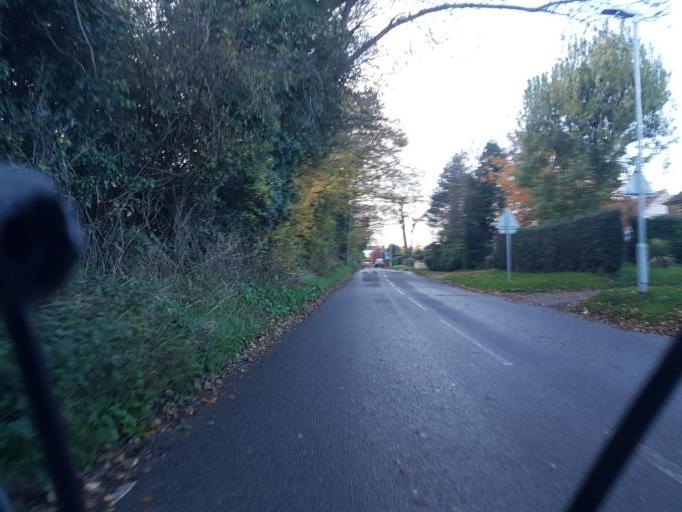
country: GB
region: England
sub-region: Kent
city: Sittingbourne
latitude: 51.3249
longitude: 0.7241
